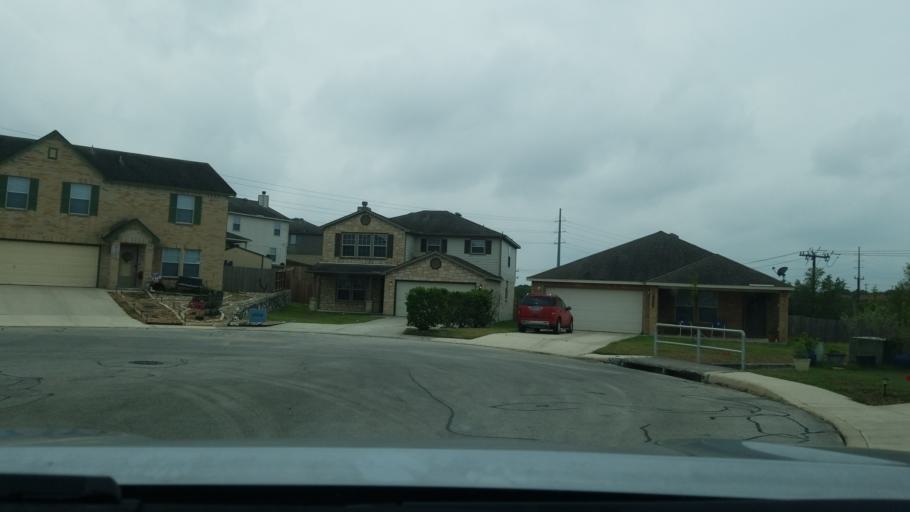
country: US
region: Texas
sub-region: Bexar County
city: Timberwood Park
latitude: 29.6811
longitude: -98.4681
